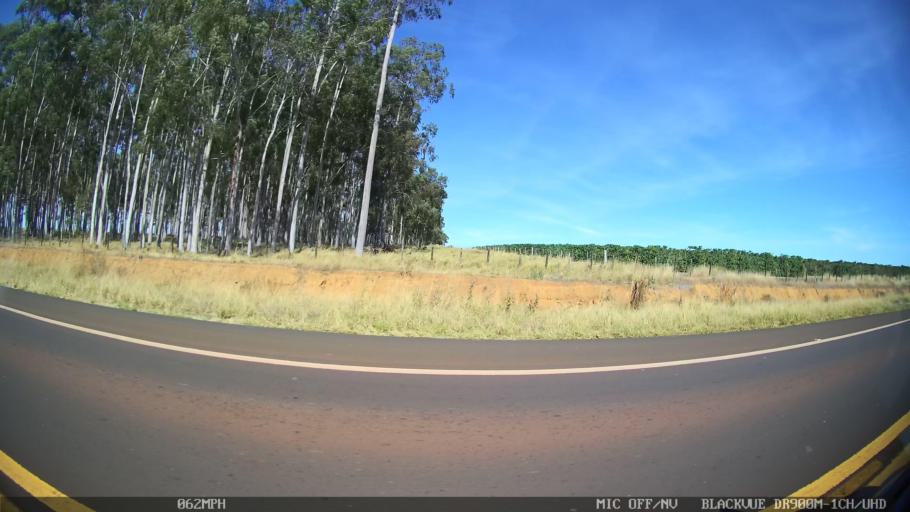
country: BR
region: Sao Paulo
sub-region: Franca
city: Franca
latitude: -20.5620
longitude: -47.5119
